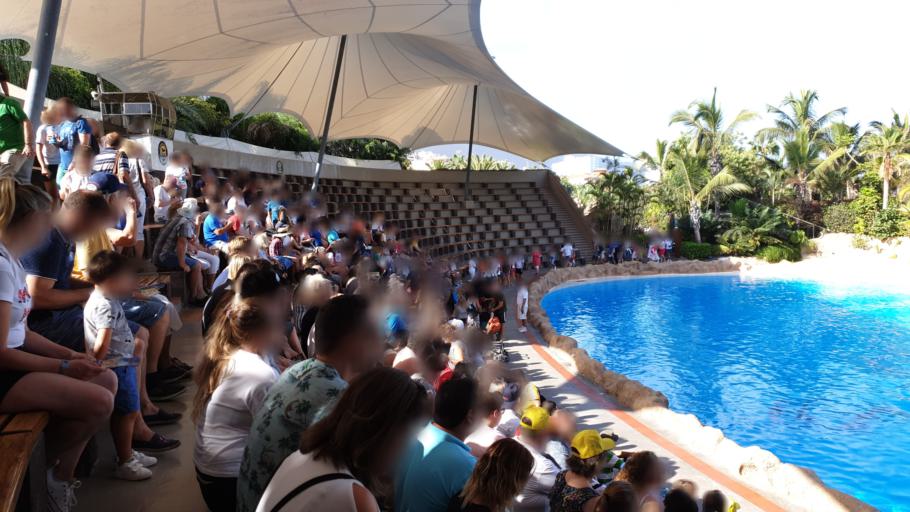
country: ES
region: Canary Islands
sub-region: Provincia de Santa Cruz de Tenerife
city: Puerto de la Cruz
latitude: 28.4087
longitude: -16.5633
